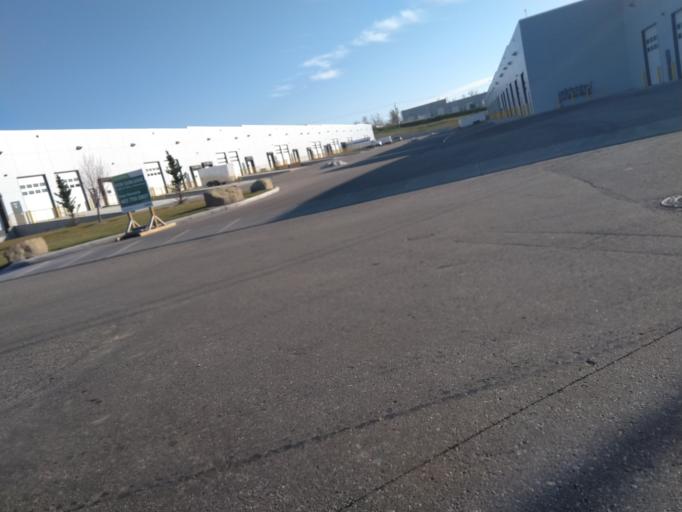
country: CA
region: Alberta
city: Calgary
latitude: 51.1056
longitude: -114.0413
